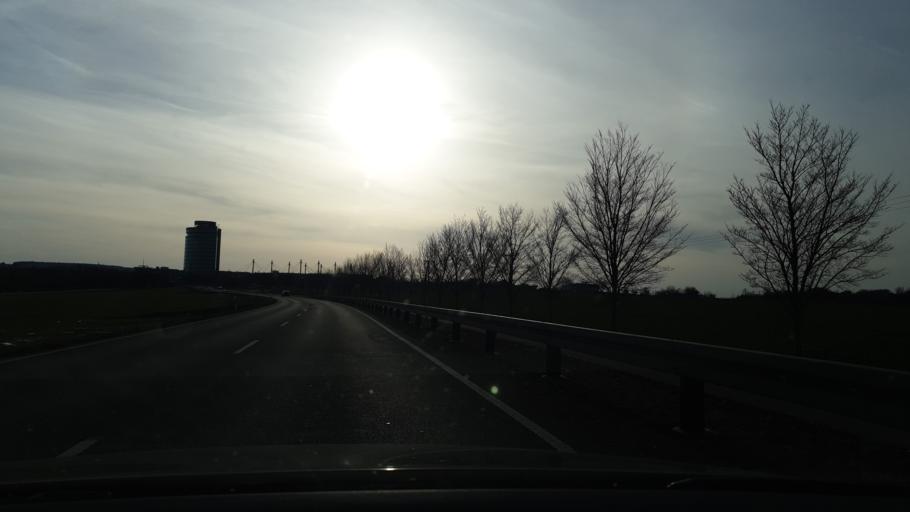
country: DE
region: Thuringia
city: Weissendorf
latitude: 50.6691
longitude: 12.0017
